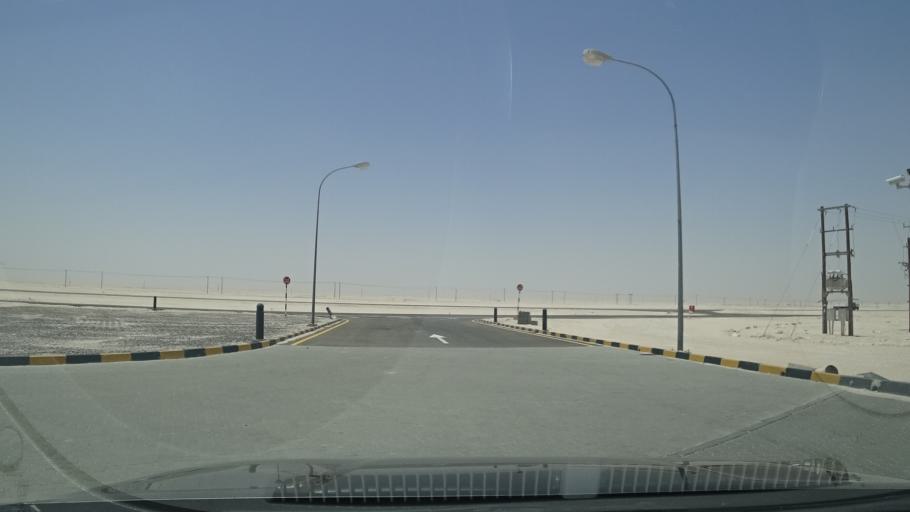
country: OM
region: Al Wusta
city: Hayma'
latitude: 19.9280
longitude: 56.2140
